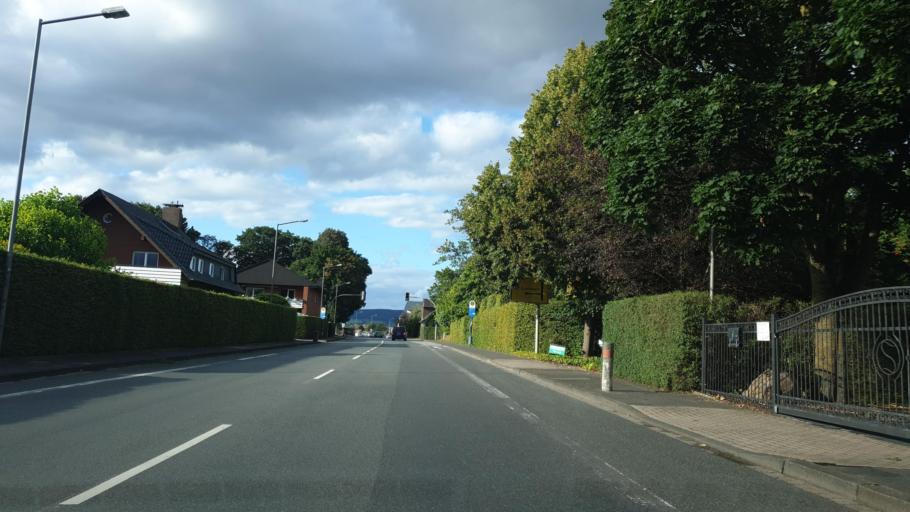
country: DE
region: North Rhine-Westphalia
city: Loehne
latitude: 52.2366
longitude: 8.7038
